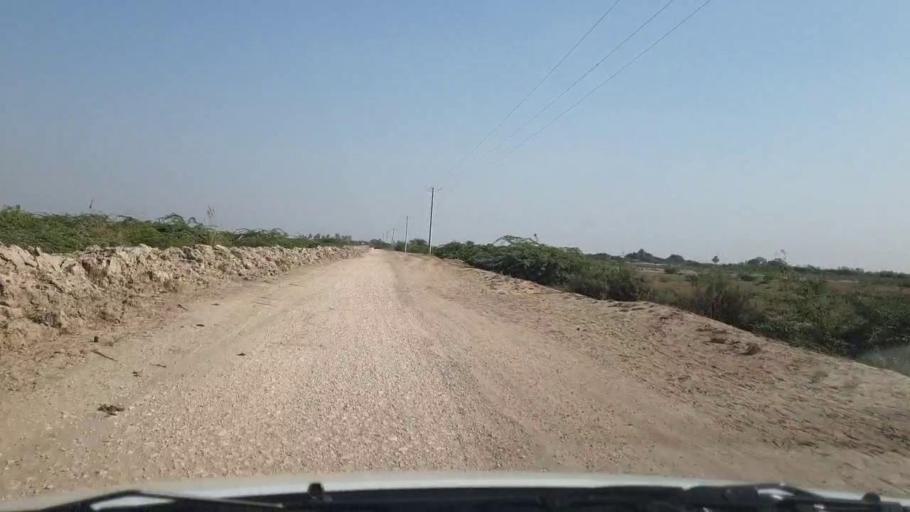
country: PK
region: Sindh
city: Mirpur Sakro
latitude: 24.6492
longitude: 67.6268
